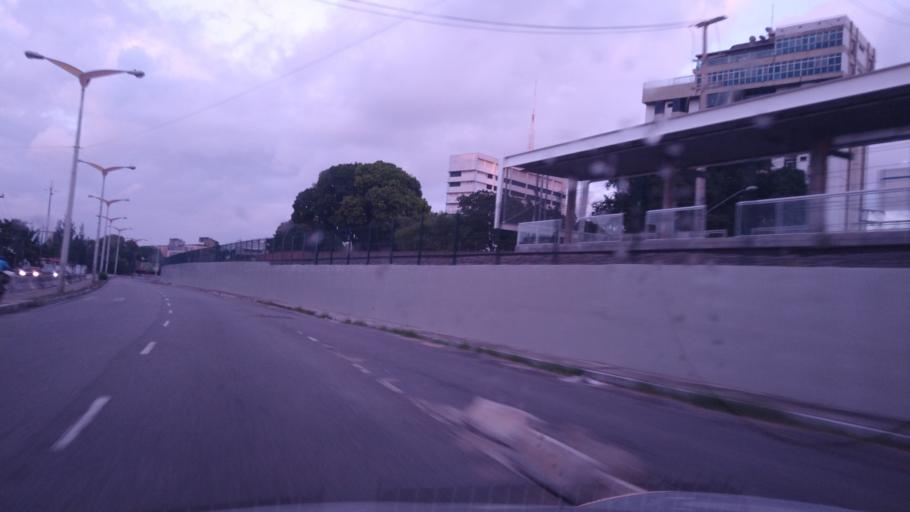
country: BR
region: Ceara
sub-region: Fortaleza
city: Fortaleza
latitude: -3.7491
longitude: -38.4937
